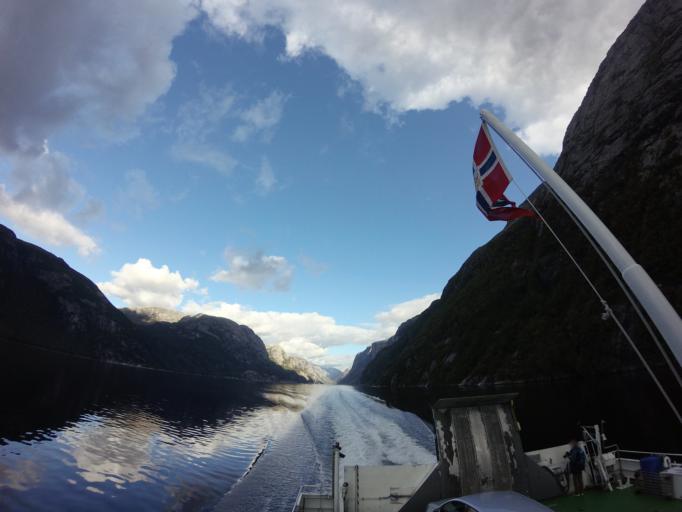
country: NO
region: Rogaland
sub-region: Hjelmeland
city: Hjelmelandsvagen
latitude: 59.0245
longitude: 6.4709
